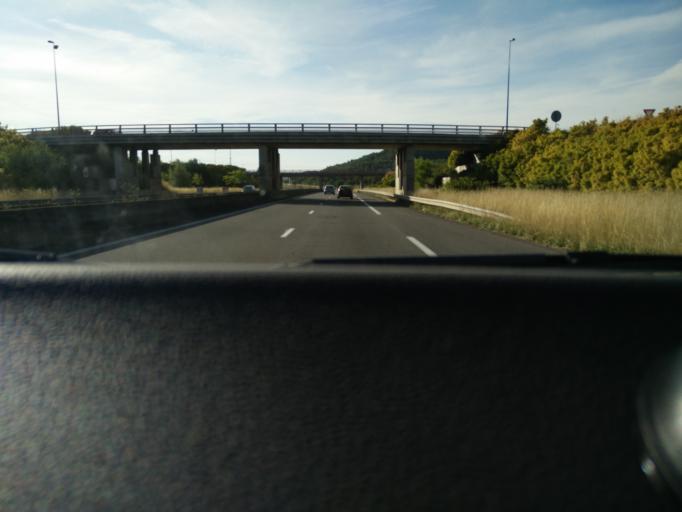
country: FR
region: Nord-Pas-de-Calais
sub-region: Departement du Nord
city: Waziers
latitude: 50.3949
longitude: 3.1186
